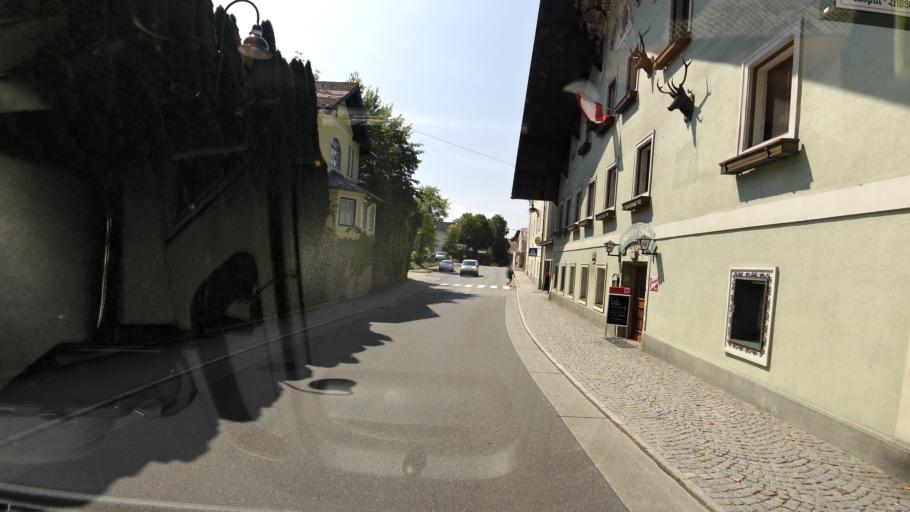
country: AT
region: Salzburg
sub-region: Politischer Bezirk Salzburg-Umgebung
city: Henndorf am Wallersee
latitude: 47.9000
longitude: 13.1893
